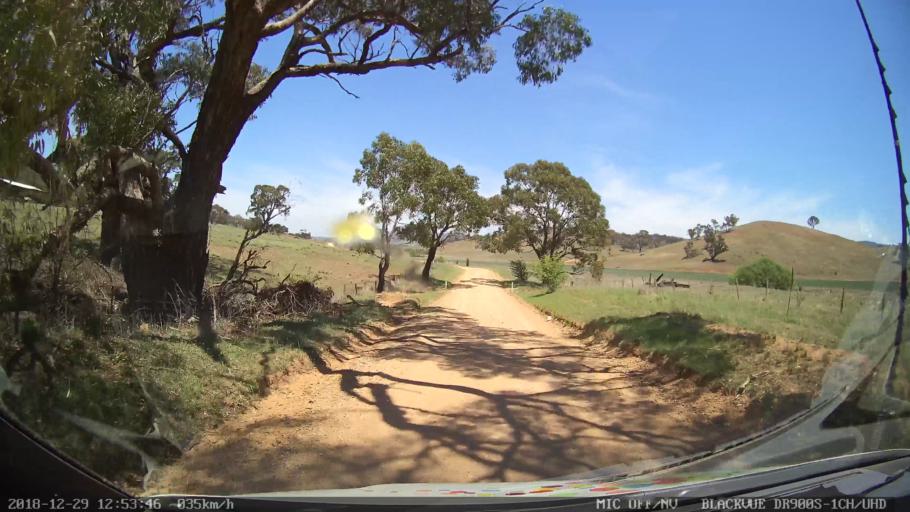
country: AU
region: Australian Capital Territory
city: Macarthur
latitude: -35.6879
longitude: 149.1885
